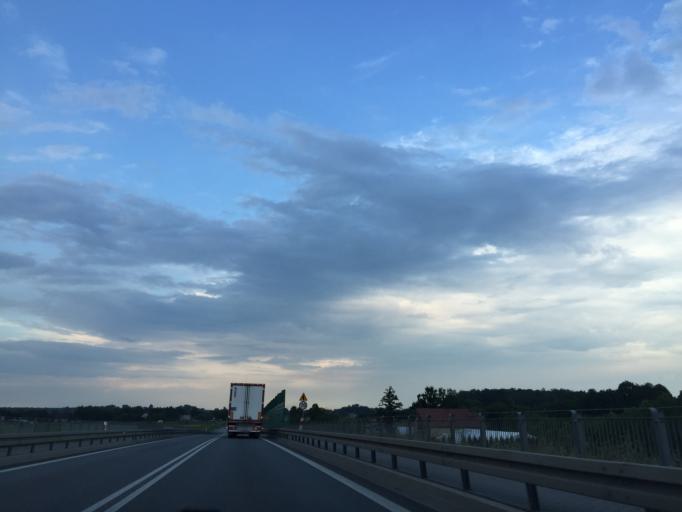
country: PL
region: Masovian Voivodeship
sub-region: Powiat minski
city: Minsk Mazowiecki
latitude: 52.2098
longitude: 21.5375
